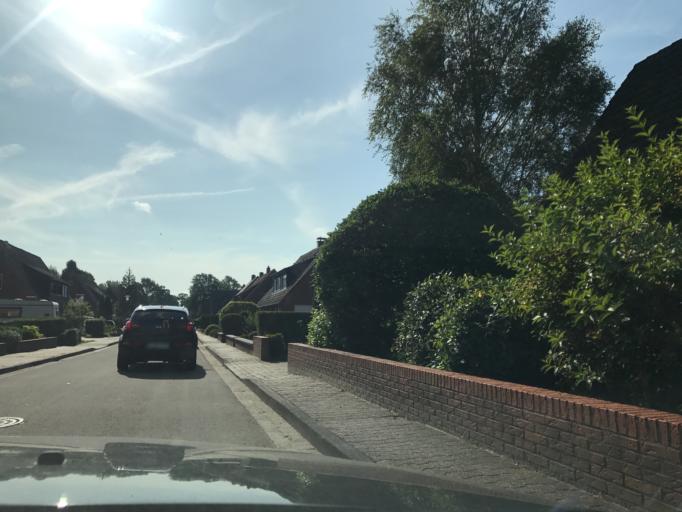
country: DE
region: Lower Saxony
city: Haselunne
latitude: 52.6809
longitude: 7.4566
